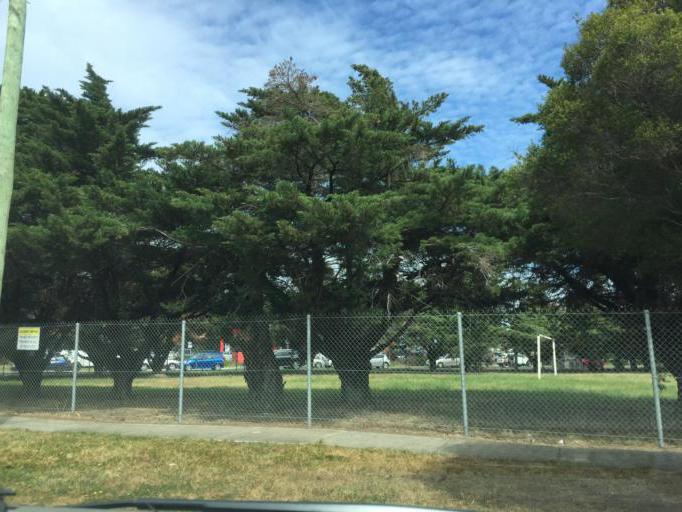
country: AU
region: Victoria
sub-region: Maribyrnong
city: Maidstone
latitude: -37.7749
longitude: 144.8803
